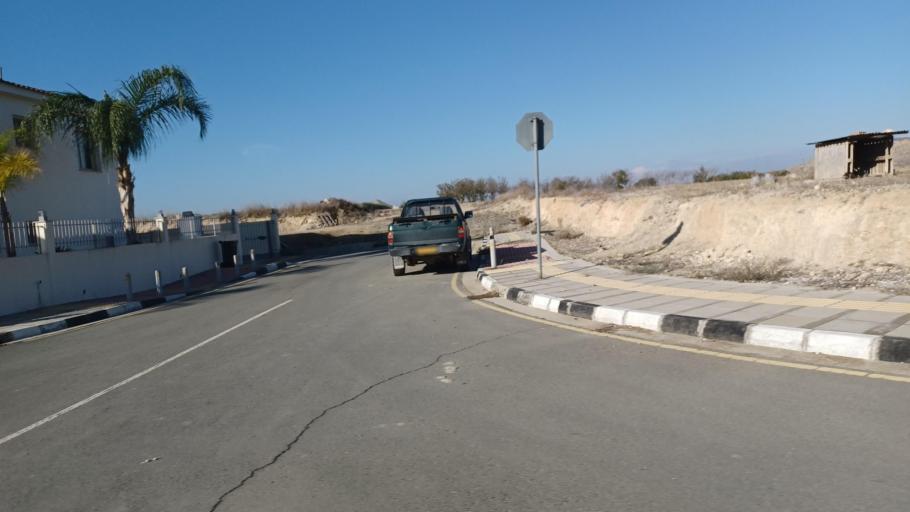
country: CY
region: Larnaka
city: Athienou
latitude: 35.0631
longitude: 33.5283
